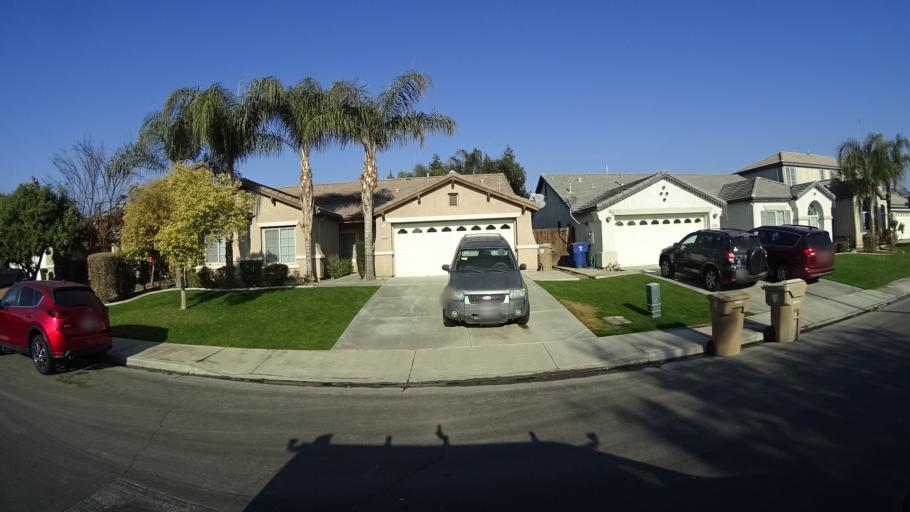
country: US
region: California
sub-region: Kern County
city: Greenacres
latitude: 35.3085
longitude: -119.1267
